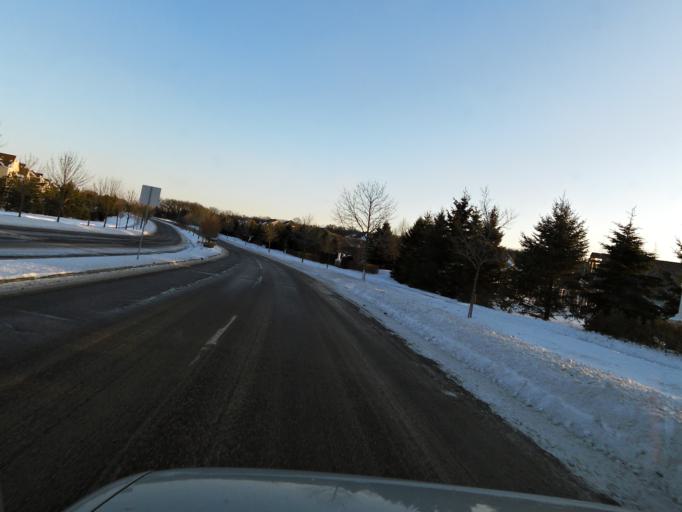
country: US
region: Minnesota
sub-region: Washington County
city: Lake Elmo
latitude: 44.9251
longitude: -92.8826
